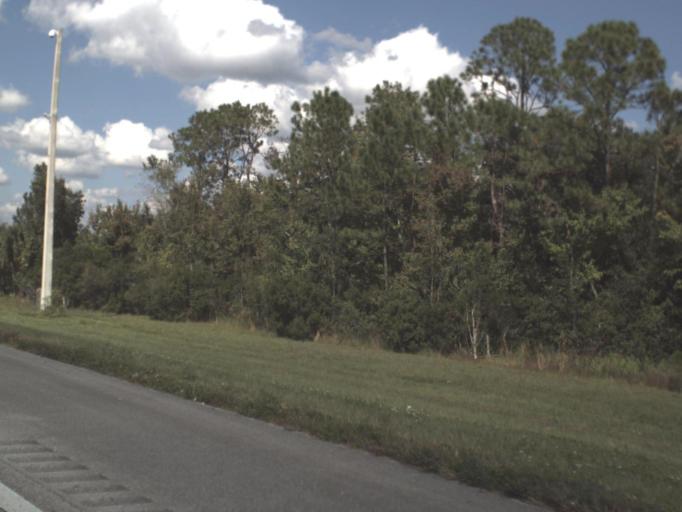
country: US
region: Florida
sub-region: Indian River County
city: Fellsmere
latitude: 27.6021
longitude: -80.8218
